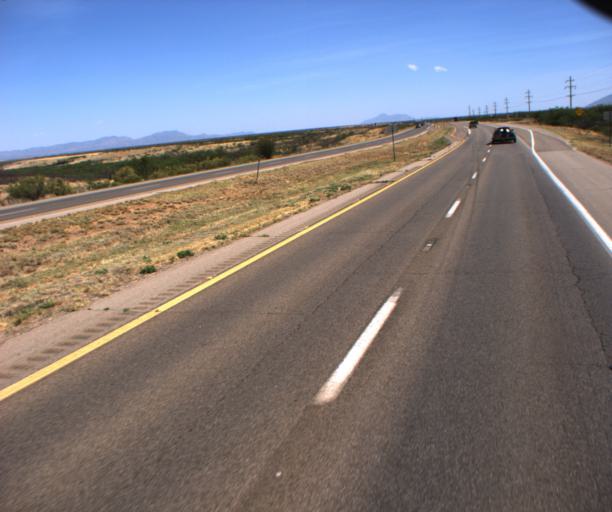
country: US
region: Arizona
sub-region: Cochise County
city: Huachuca City
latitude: 31.6584
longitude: -110.3487
